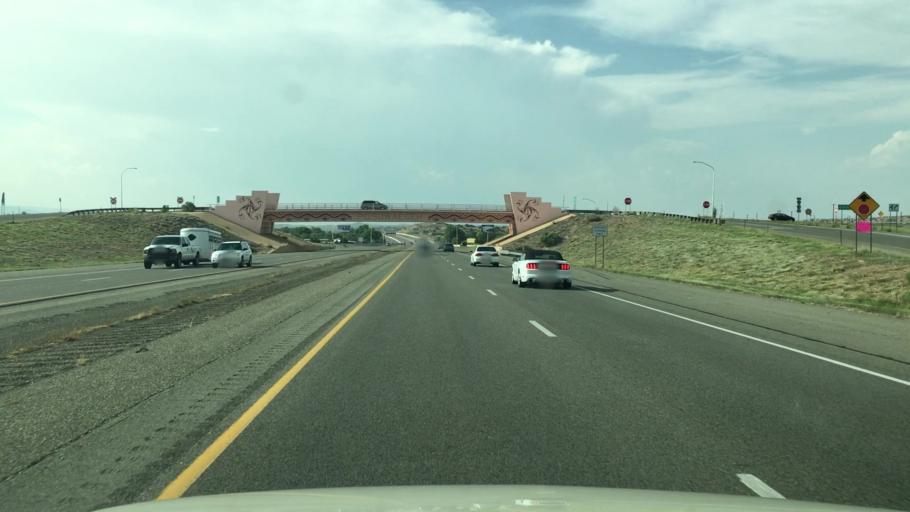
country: US
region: New Mexico
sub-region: Santa Fe County
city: Nambe
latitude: 35.8579
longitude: -105.9986
